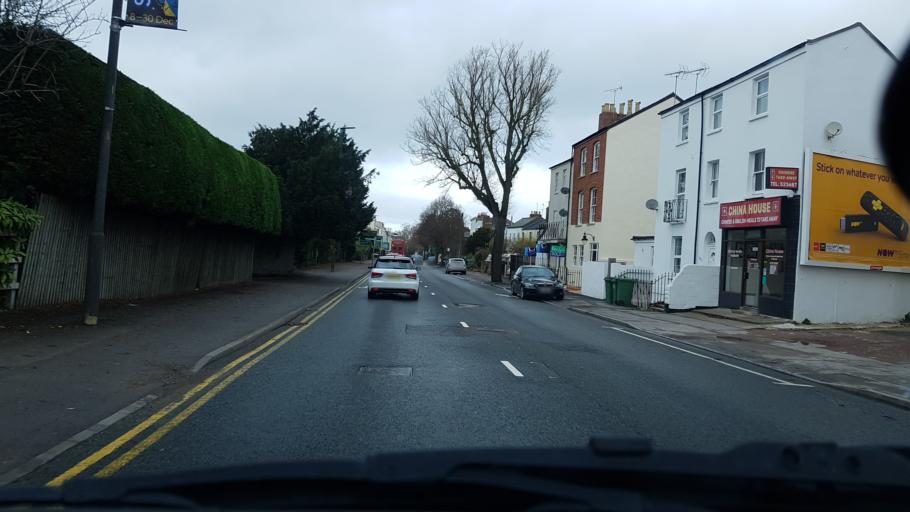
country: GB
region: England
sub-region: Gloucestershire
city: Charlton Kings
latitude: 51.8913
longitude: -2.0614
